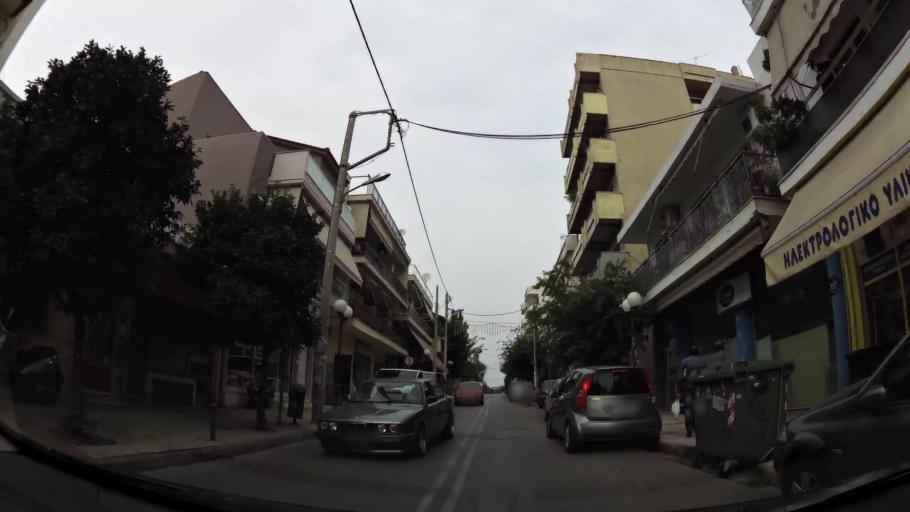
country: GR
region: Attica
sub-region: Nomarchia Athinas
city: Nea Ionia
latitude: 38.0350
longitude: 23.7551
